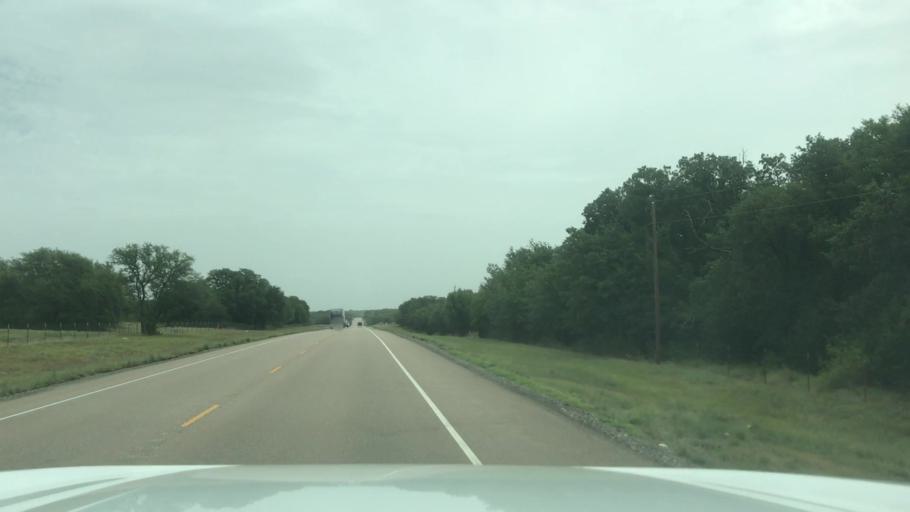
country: US
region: Texas
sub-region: Hamilton County
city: Hico
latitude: 31.9780
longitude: -97.9072
